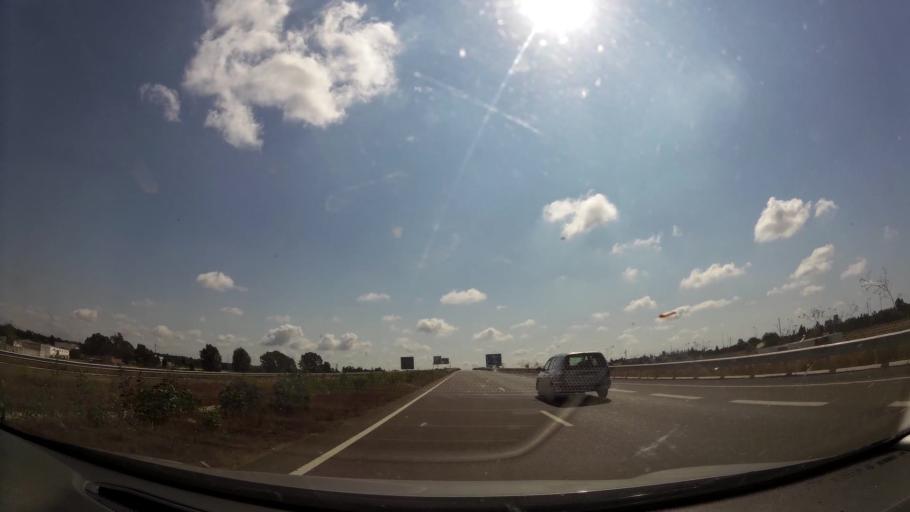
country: MA
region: Rabat-Sale-Zemmour-Zaer
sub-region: Skhirate-Temara
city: Temara
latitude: 33.8451
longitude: -6.8423
